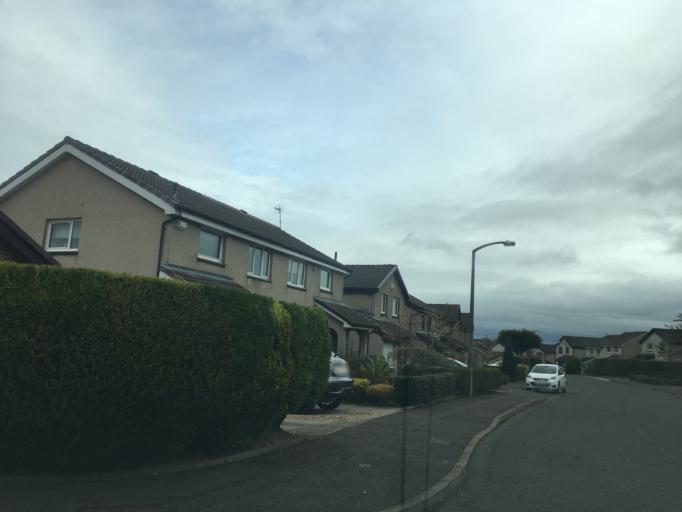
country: GB
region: Scotland
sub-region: Edinburgh
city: Colinton
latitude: 55.9007
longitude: -3.2235
